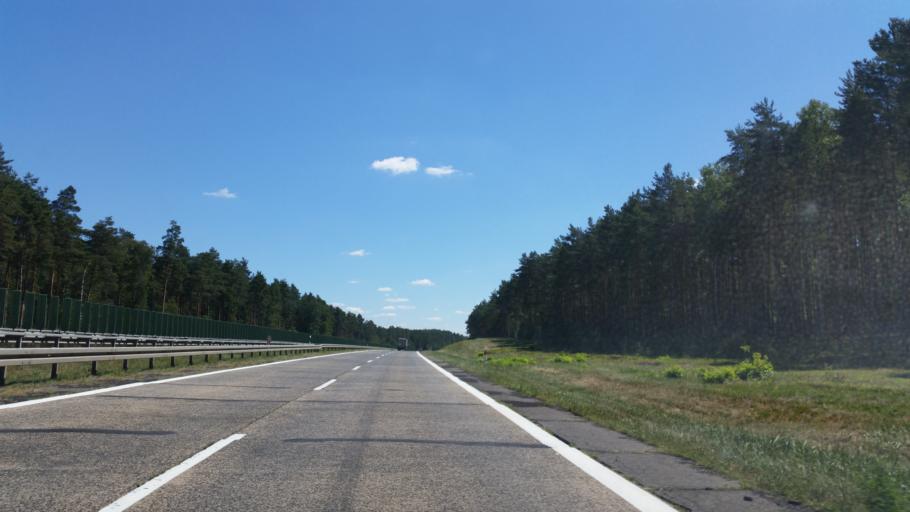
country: PL
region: Lubusz
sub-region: Powiat zaganski
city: Malomice
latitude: 51.4172
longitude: 15.4824
